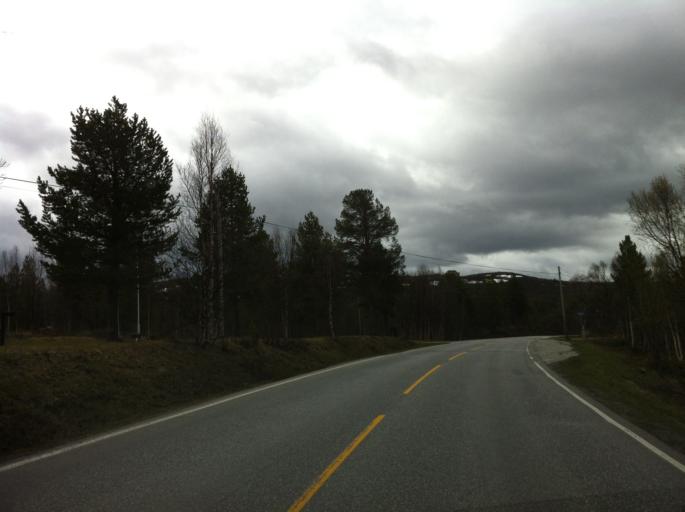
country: NO
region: Sor-Trondelag
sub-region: Roros
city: Roros
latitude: 62.6169
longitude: 11.8447
